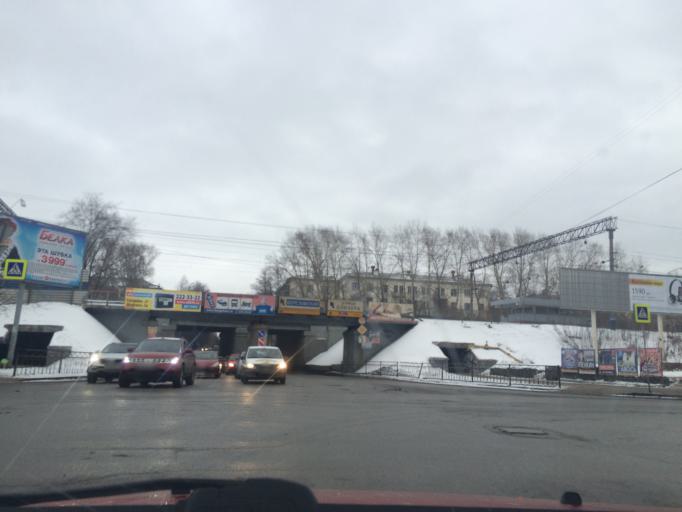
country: RU
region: Sverdlovsk
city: Yekaterinburg
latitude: 56.8439
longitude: 60.6308
